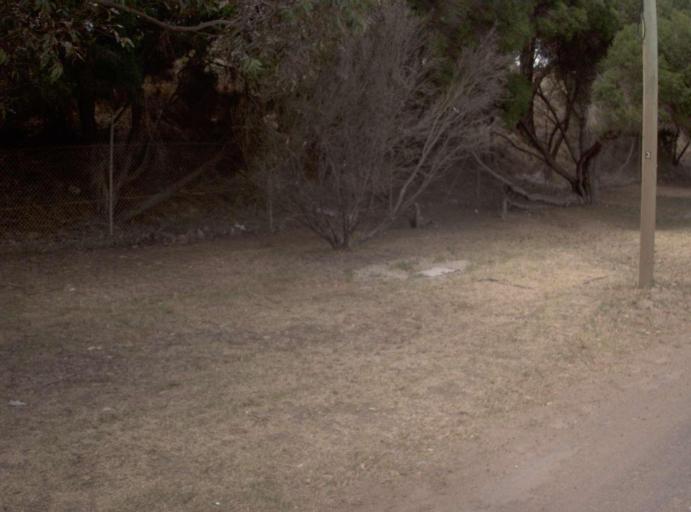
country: AU
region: Victoria
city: Heatherton
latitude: -37.9530
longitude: 145.0991
